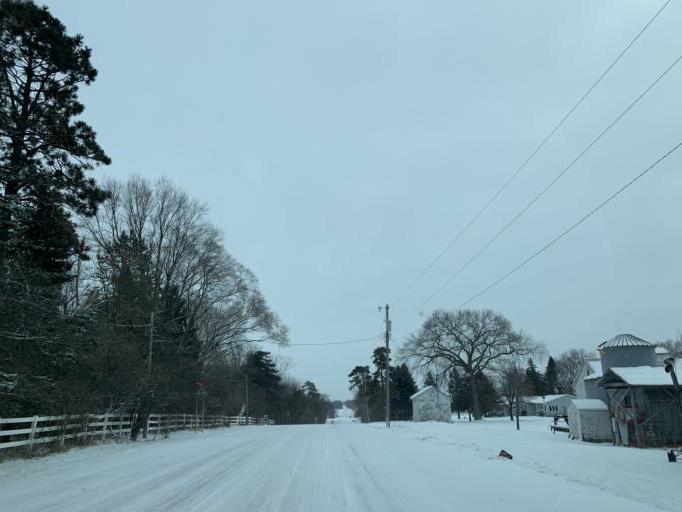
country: US
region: Minnesota
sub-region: Washington County
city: Cottage Grove
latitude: 44.8604
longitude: -92.9218
